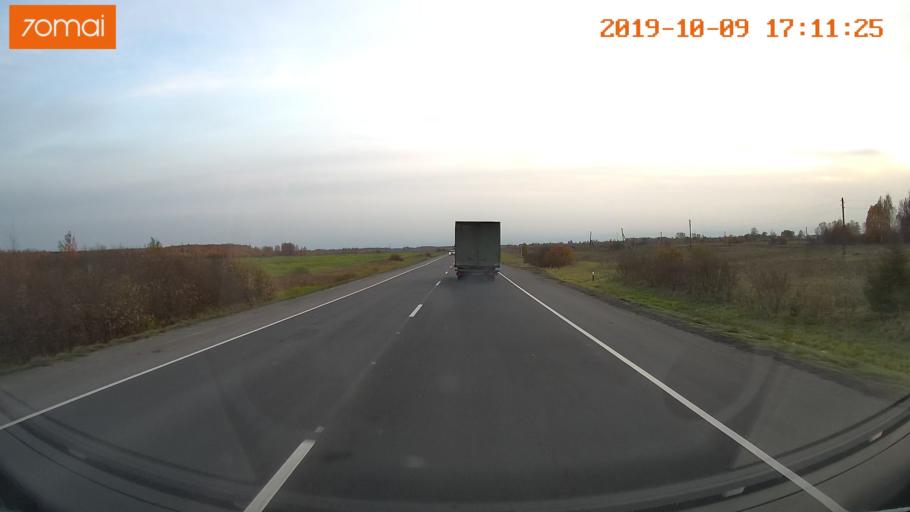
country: RU
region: Ivanovo
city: Privolzhsk
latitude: 57.3428
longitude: 41.2501
